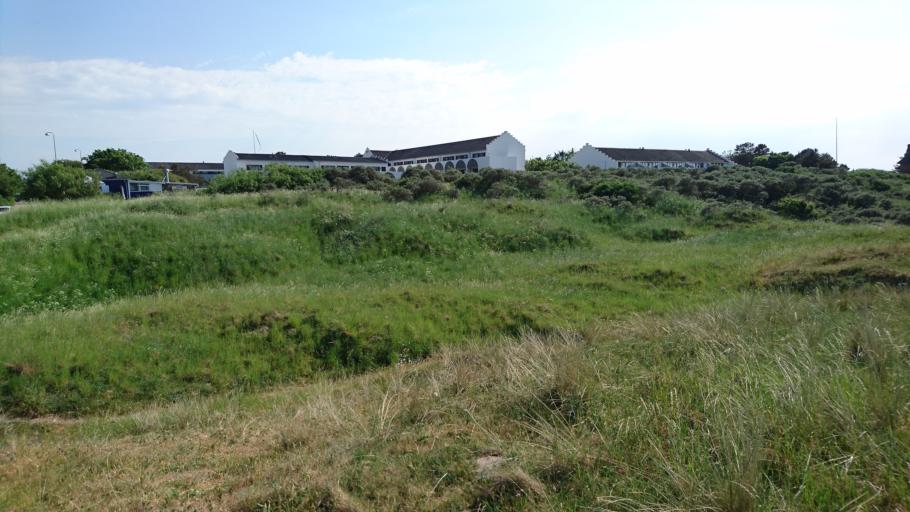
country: DK
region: North Denmark
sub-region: Hjorring Kommune
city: Sindal
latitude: 57.5945
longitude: 10.1842
